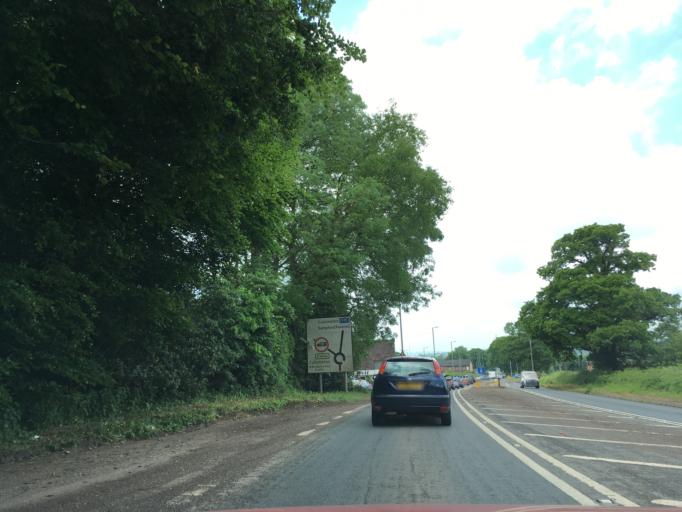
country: GB
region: England
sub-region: Devon
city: Uffculme
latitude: 50.9177
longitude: -3.3417
